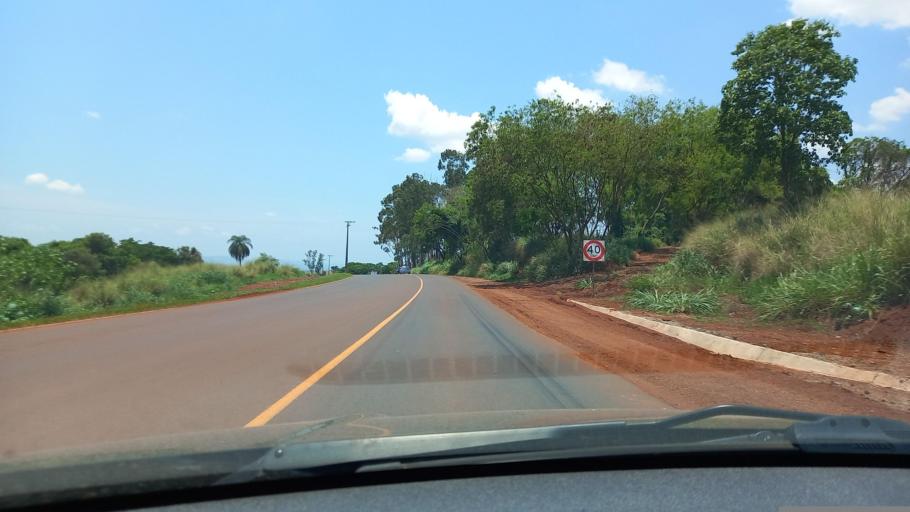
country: BR
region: Sao Paulo
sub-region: Moji-Guacu
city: Mogi-Gaucu
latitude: -22.3424
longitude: -46.8808
